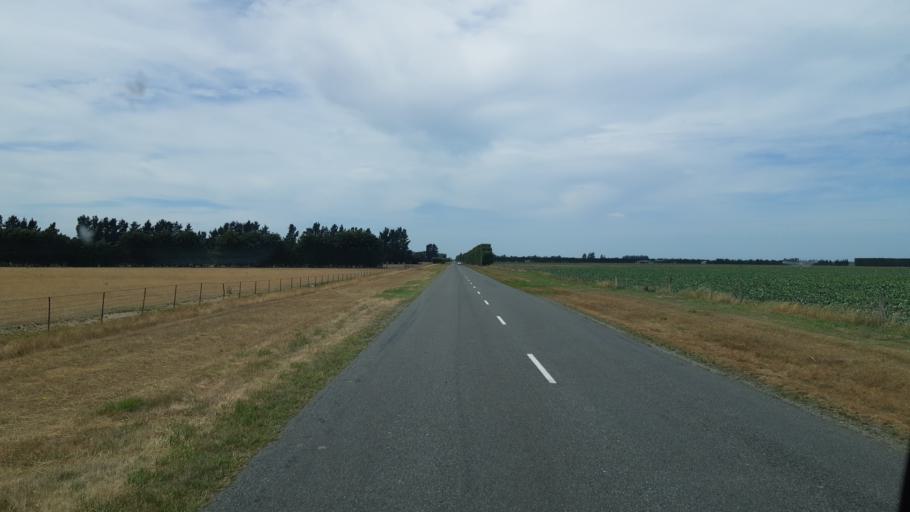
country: NZ
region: Canterbury
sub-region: Ashburton District
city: Tinwald
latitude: -43.9285
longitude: 171.5865
